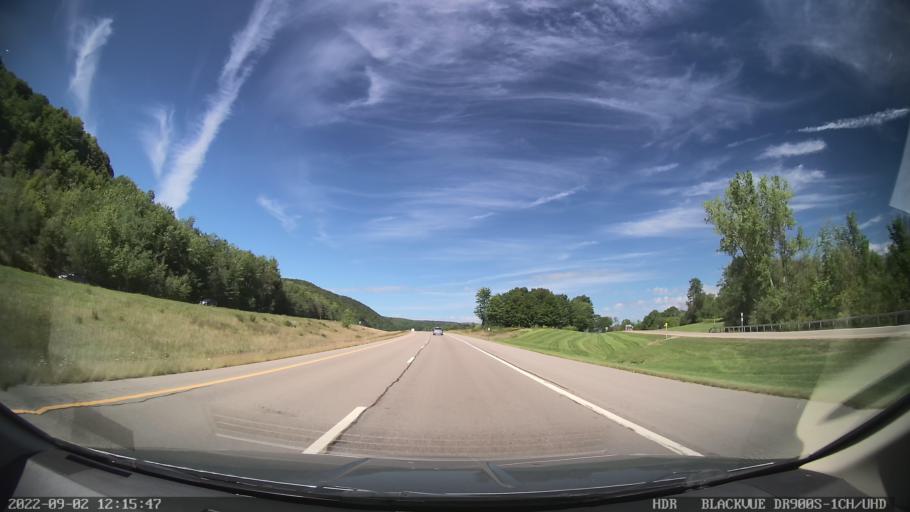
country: US
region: New York
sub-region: Steuben County
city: Wayland
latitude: 42.4731
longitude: -77.4912
